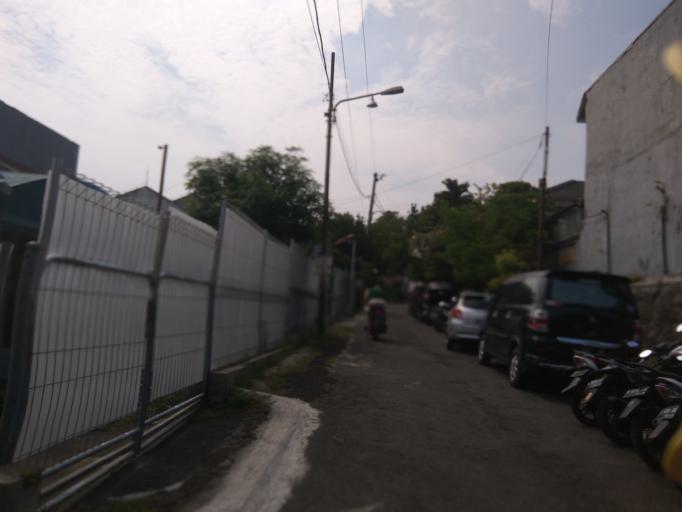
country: ID
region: Central Java
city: Semarang
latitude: -7.0449
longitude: 110.4184
